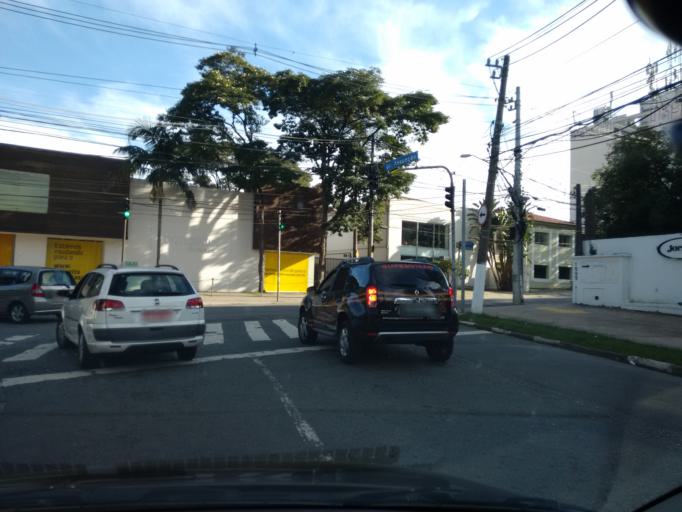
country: BR
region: Sao Paulo
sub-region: Sao Paulo
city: Sao Paulo
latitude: -23.5728
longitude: -46.6817
